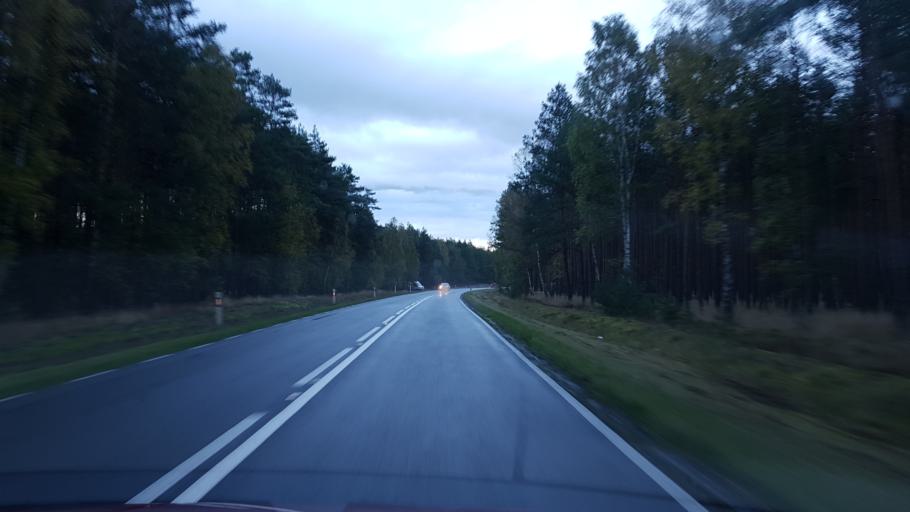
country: PL
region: Greater Poland Voivodeship
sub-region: Powiat pilski
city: Pila
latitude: 53.1970
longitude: 16.8282
